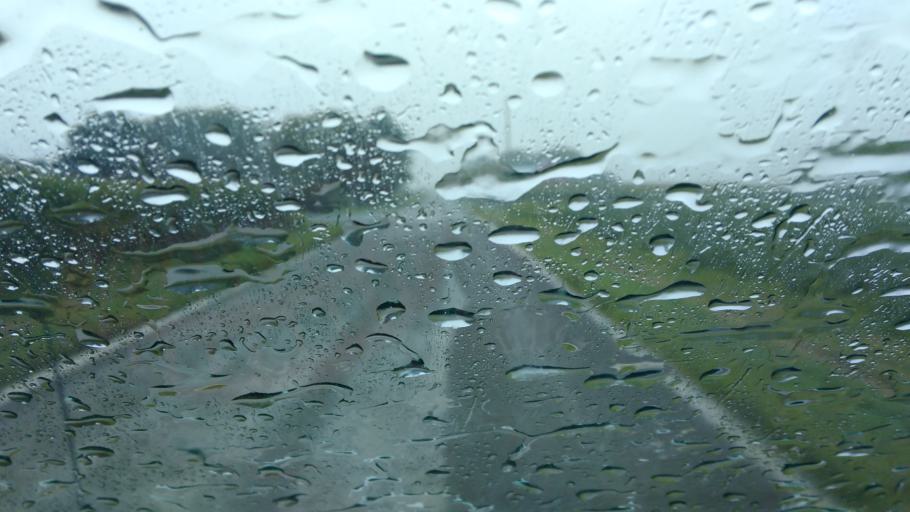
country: US
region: Ohio
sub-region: Hardin County
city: Kenton
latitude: 40.7012
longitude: -83.5379
